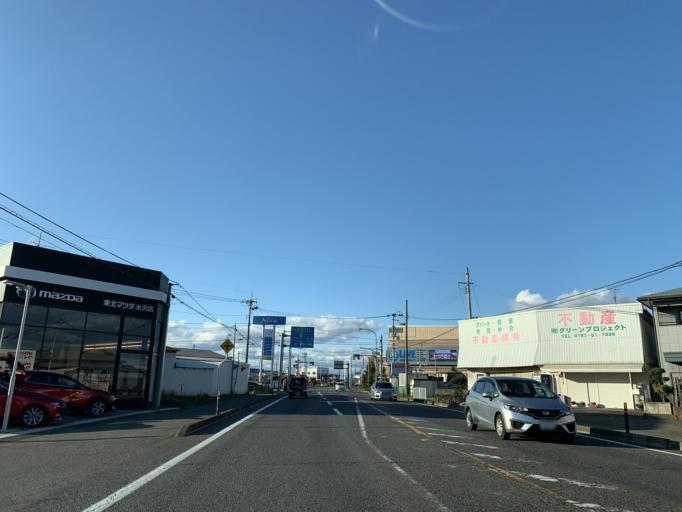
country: JP
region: Iwate
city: Mizusawa
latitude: 39.1557
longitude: 141.1469
